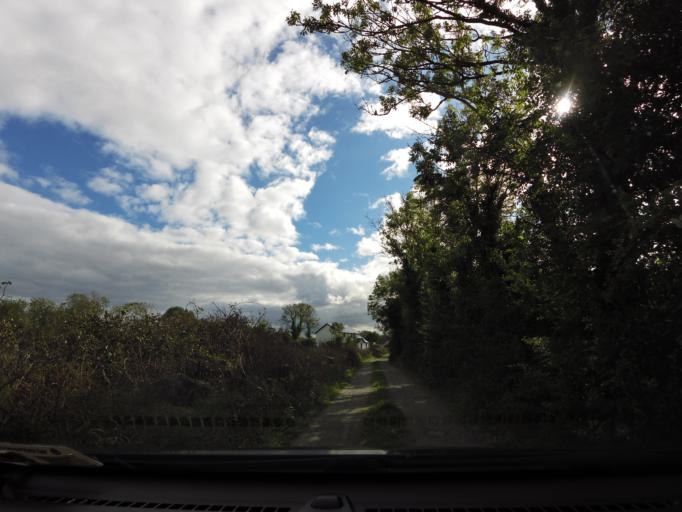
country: IE
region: Connaught
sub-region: County Galway
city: Moycullen
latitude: 53.3549
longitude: -9.1578
